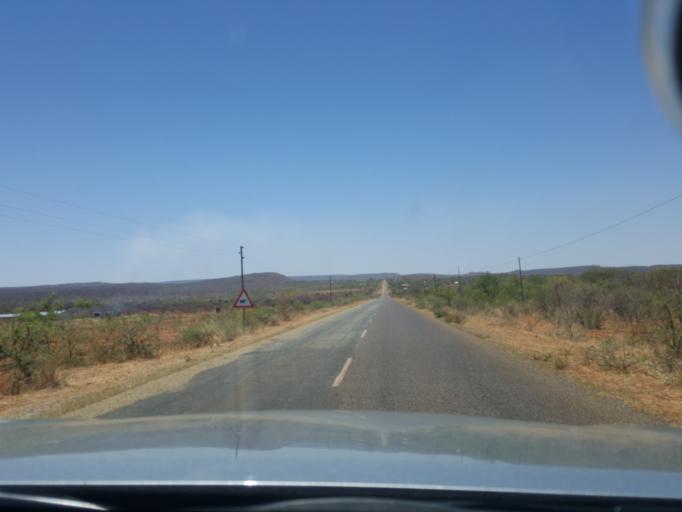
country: ZA
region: North-West
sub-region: Ngaka Modiri Molema District Municipality
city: Zeerust
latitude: -25.3945
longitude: 25.9381
